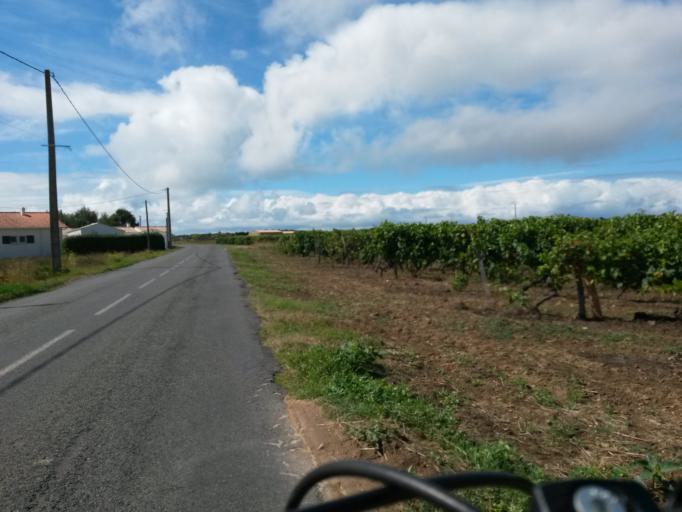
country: FR
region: Poitou-Charentes
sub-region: Departement de la Charente-Maritime
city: Dolus-d'Oleron
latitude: 45.9407
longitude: -1.3361
